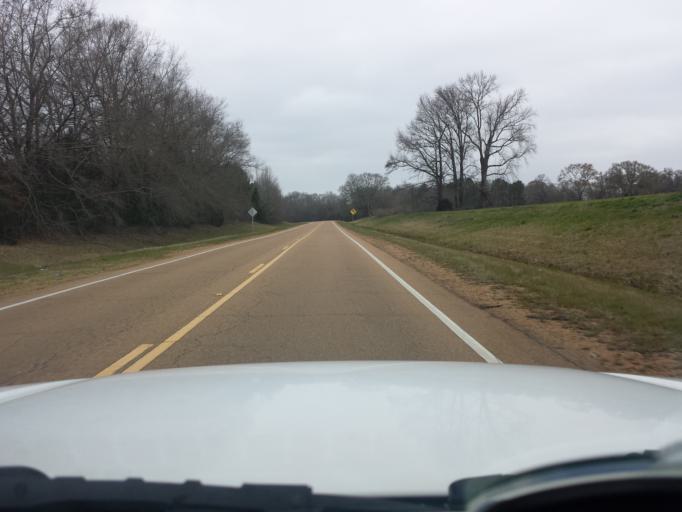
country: US
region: Mississippi
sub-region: Yazoo County
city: Yazoo City
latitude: 32.7865
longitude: -90.2013
